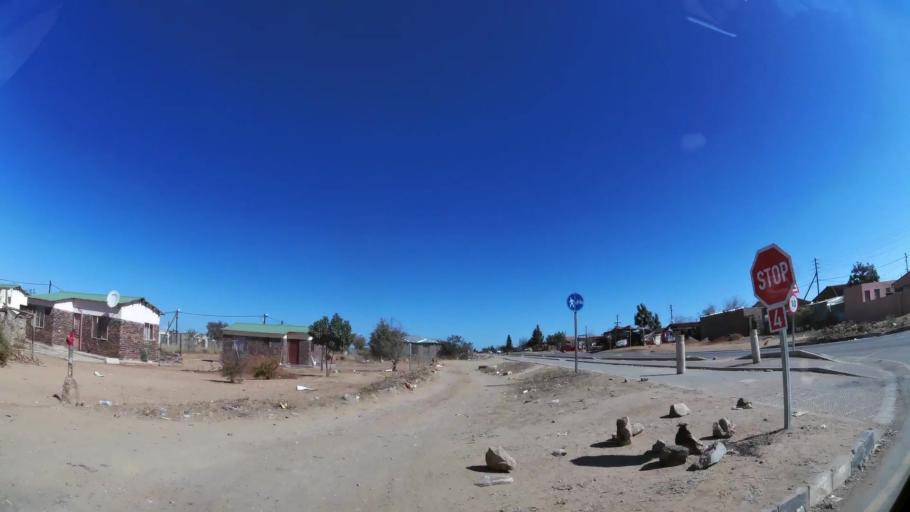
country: ZA
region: Limpopo
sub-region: Capricorn District Municipality
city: Polokwane
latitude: -23.8941
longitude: 29.4181
